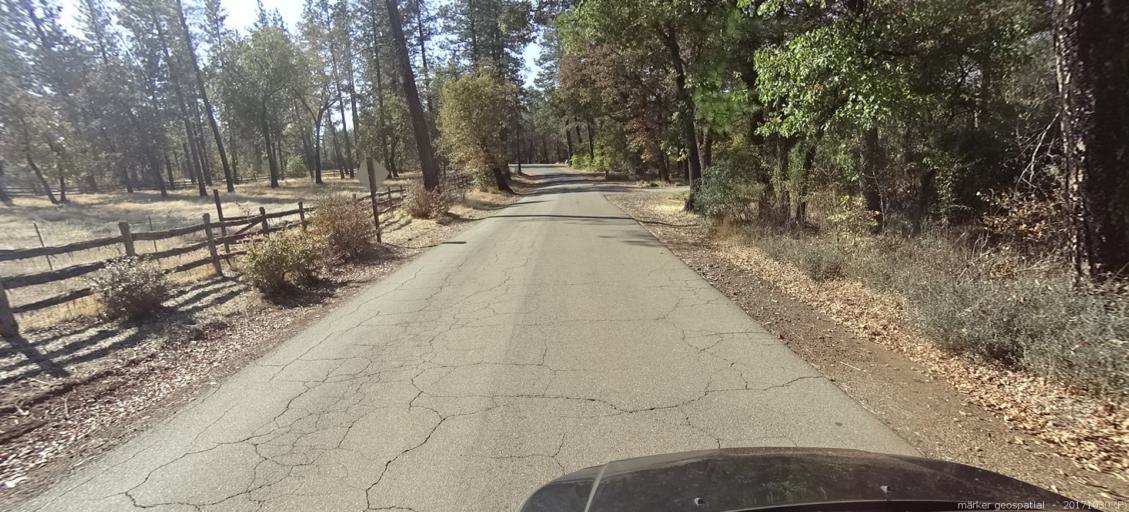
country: US
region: California
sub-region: Shasta County
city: Shingletown
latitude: 40.5071
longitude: -122.0001
